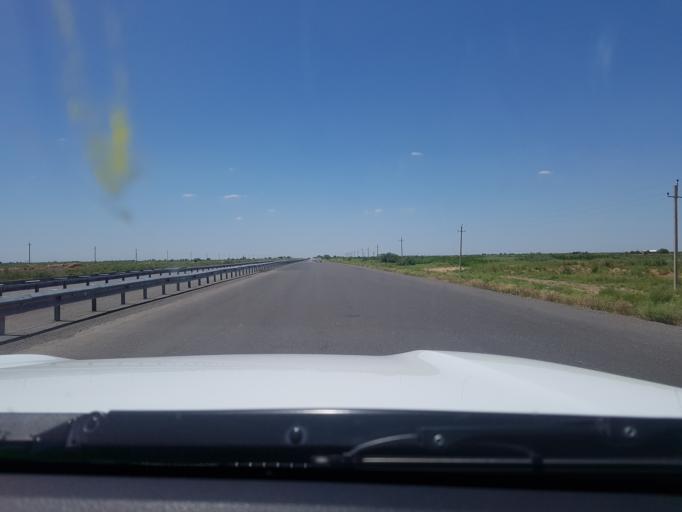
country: IR
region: Razavi Khorasan
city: Sarakhs
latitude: 37.2243
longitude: 61.2154
